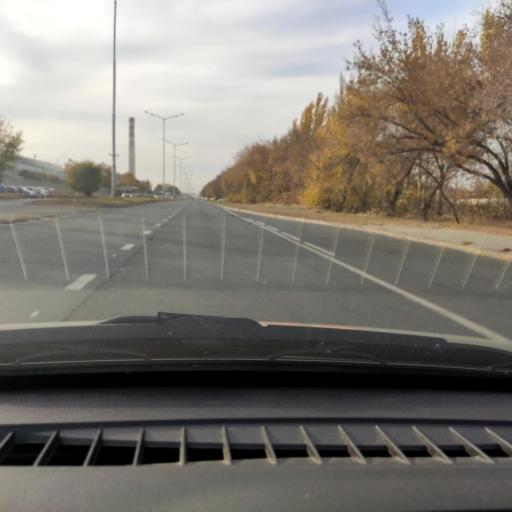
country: RU
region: Samara
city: Tol'yatti
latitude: 53.5690
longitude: 49.2645
